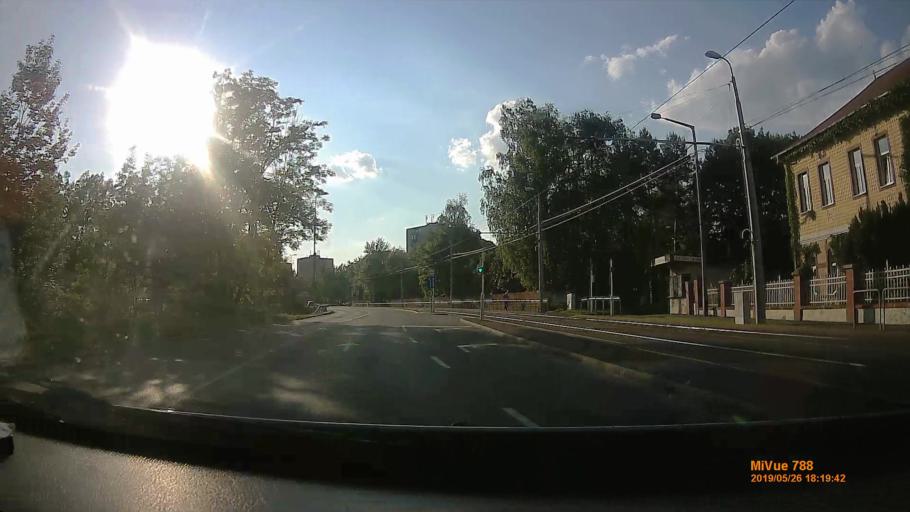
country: HU
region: Borsod-Abauj-Zemplen
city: Sajobabony
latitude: 48.1060
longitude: 20.6804
